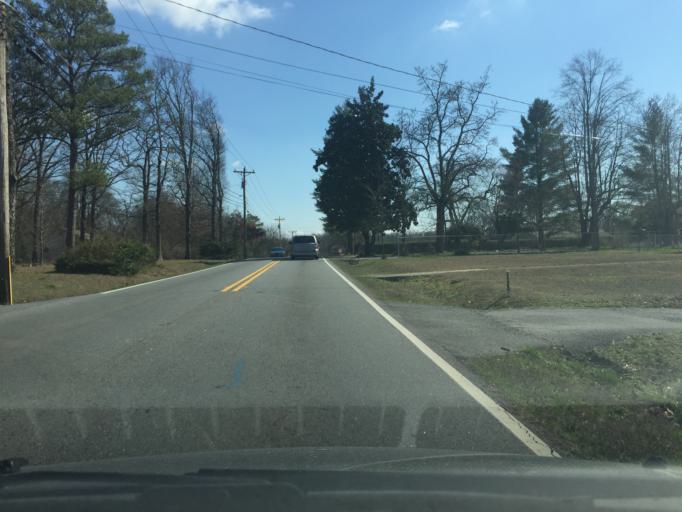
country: US
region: Georgia
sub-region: Catoosa County
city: Fort Oglethorpe
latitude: 34.9594
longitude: -85.2462
